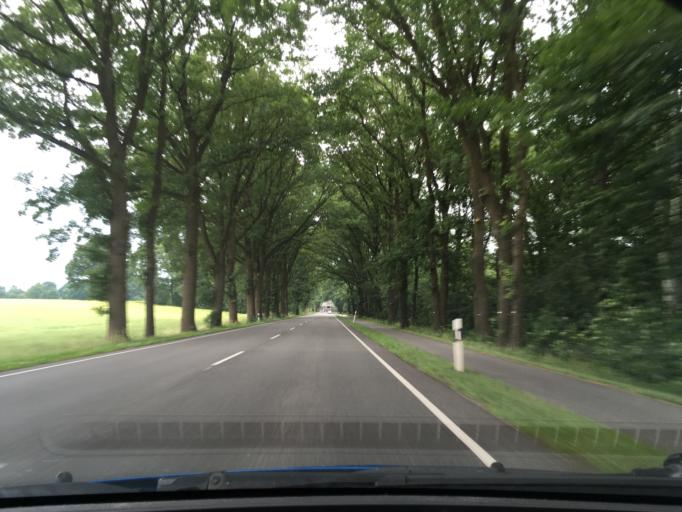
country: DE
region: Lower Saxony
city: Appel
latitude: 53.3944
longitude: 9.7924
